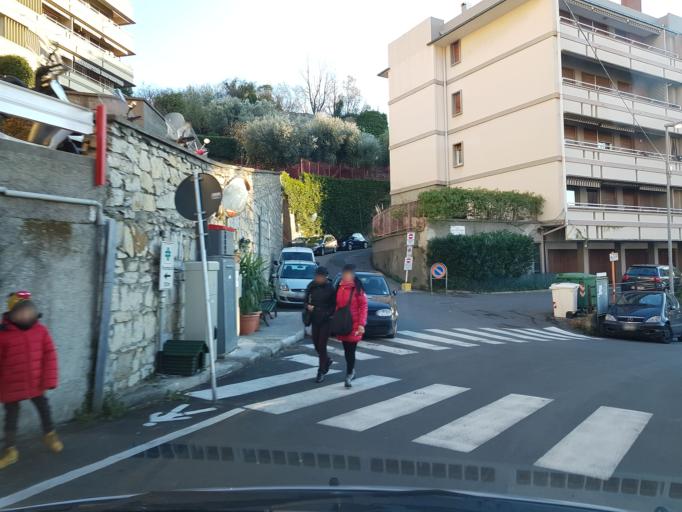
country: IT
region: Liguria
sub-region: Provincia di Genova
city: Genoa
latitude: 44.4080
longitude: 8.9826
